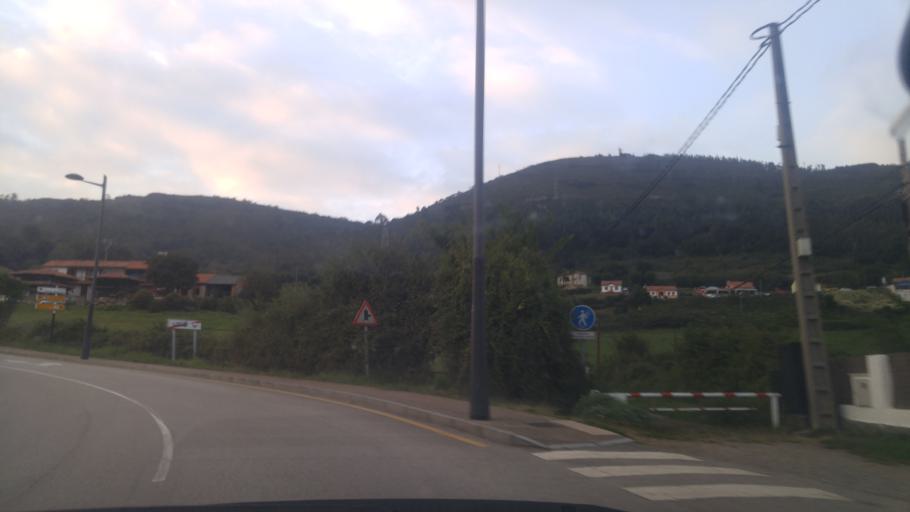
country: ES
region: Asturias
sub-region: Province of Asturias
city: Oviedo
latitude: 43.3759
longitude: -5.8645
